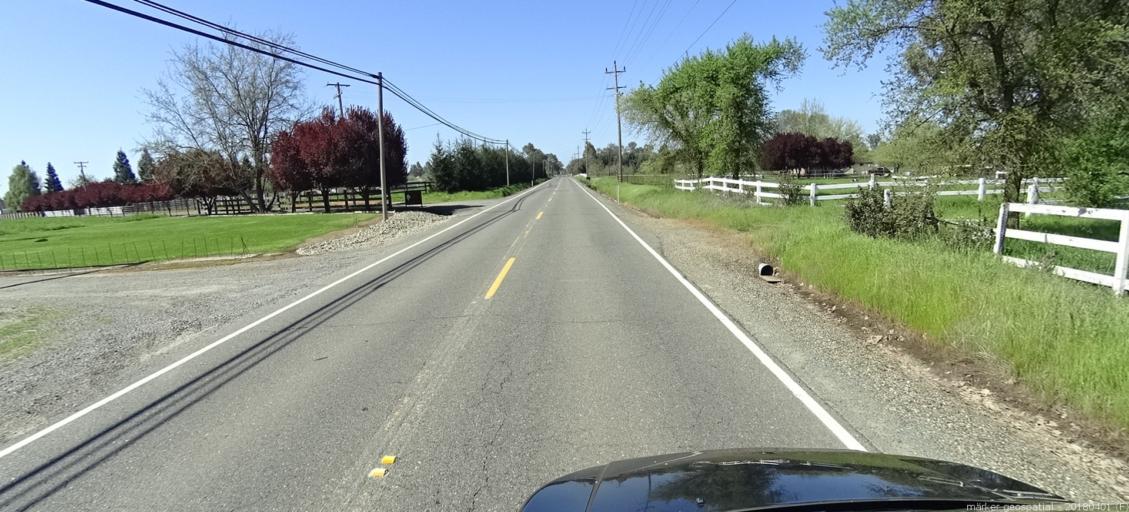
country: US
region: California
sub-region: Sacramento County
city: Wilton
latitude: 38.4135
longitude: -121.2351
